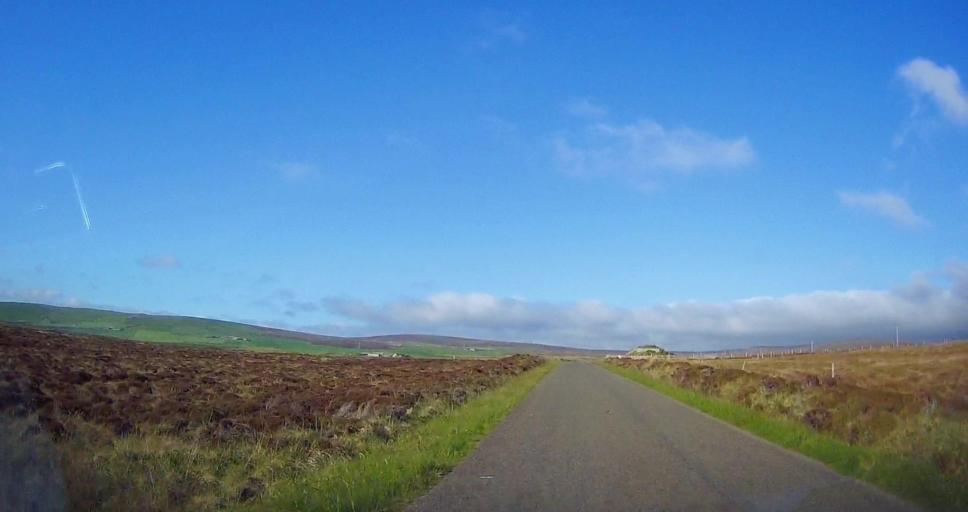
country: GB
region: Scotland
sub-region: Orkney Islands
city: Stromness
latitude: 59.0791
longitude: -3.1991
